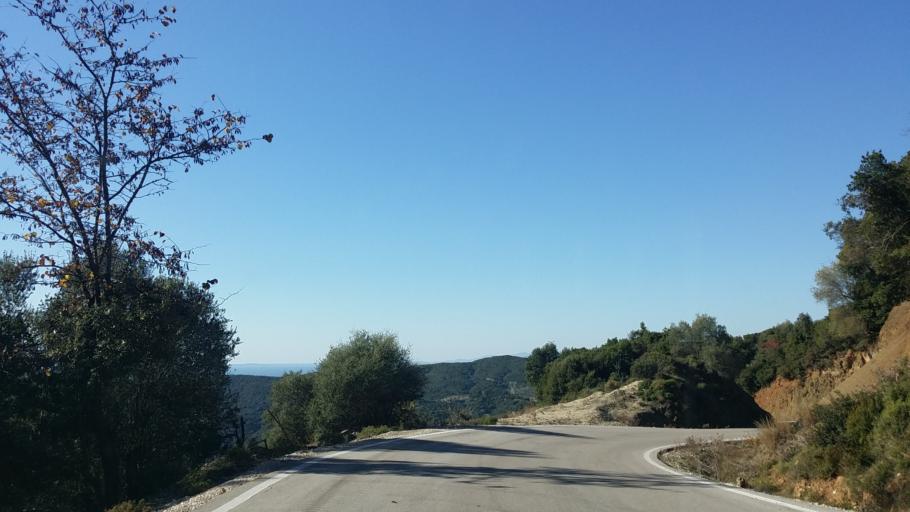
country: GR
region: West Greece
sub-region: Nomos Aitolias kai Akarnanias
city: Krikellos
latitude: 38.9654
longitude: 21.2355
